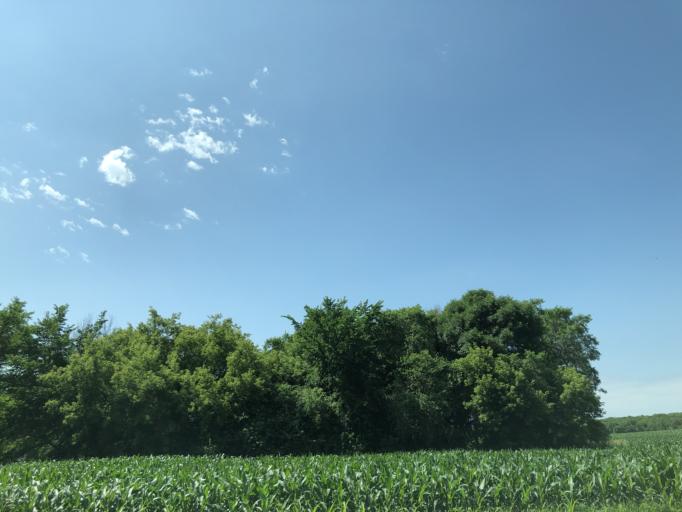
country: US
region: Minnesota
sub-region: Douglas County
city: Alexandria
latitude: 45.9383
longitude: -95.3797
